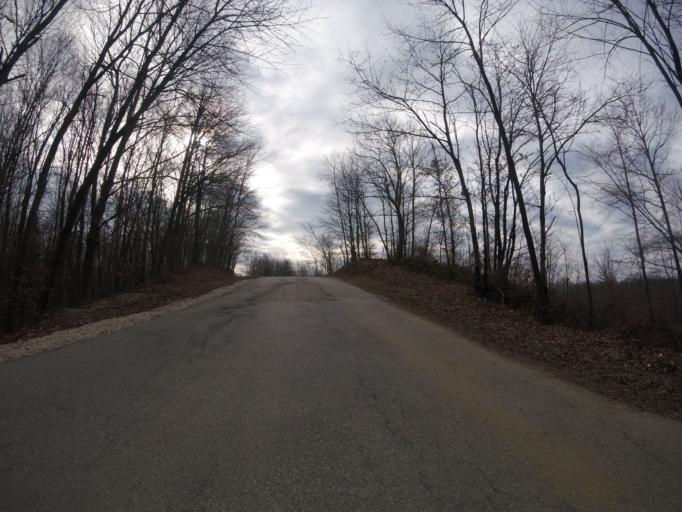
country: HR
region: Zagrebacka
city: Mraclin
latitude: 45.5193
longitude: 16.0493
